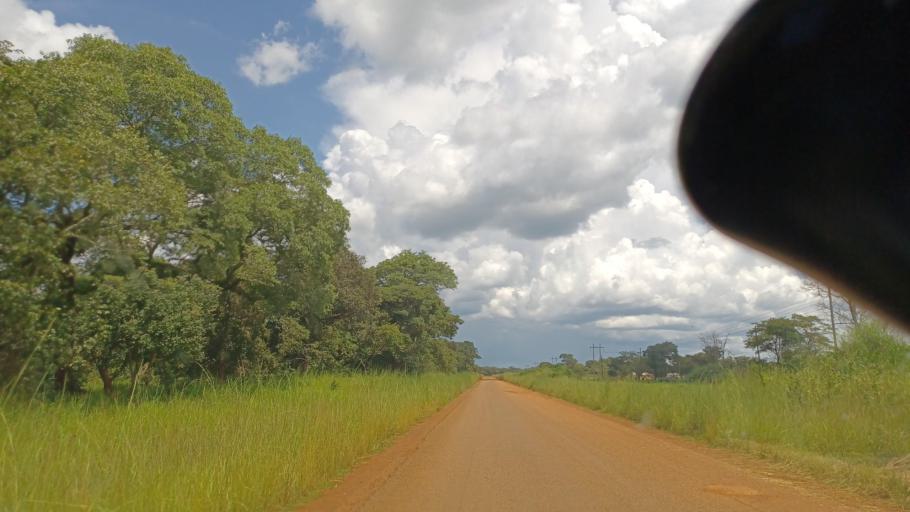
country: ZM
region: North-Western
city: Solwezi
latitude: -12.6868
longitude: 26.0405
